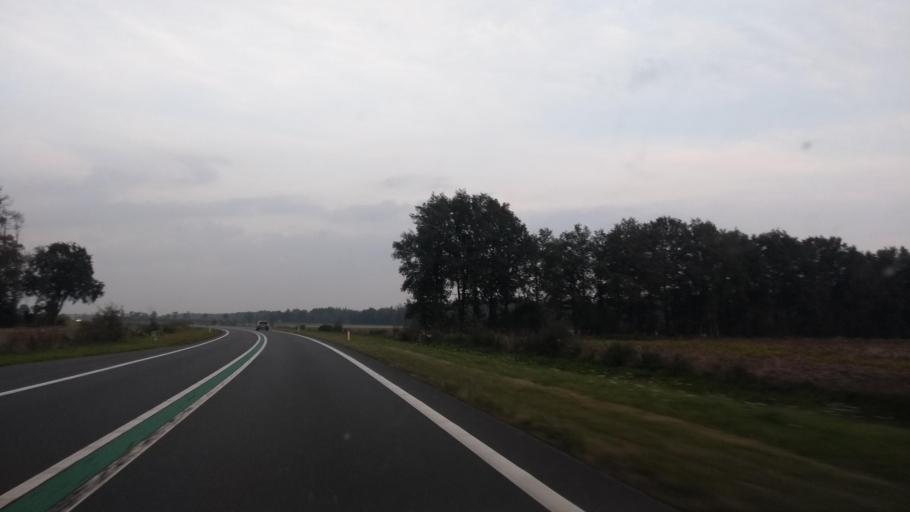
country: NL
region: Overijssel
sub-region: Gemeente Twenterand
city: Den Ham
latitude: 52.5498
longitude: 6.4285
